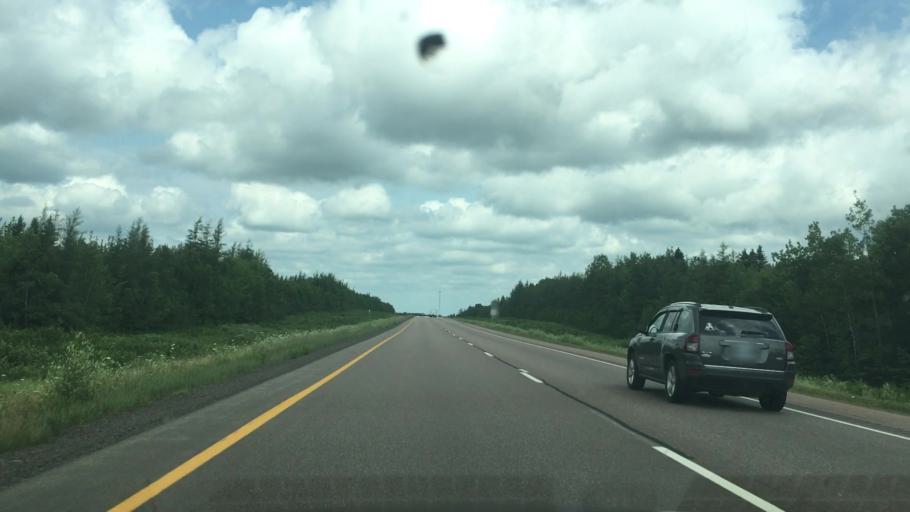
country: CA
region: New Brunswick
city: Dieppe
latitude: 46.0586
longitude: -64.5871
